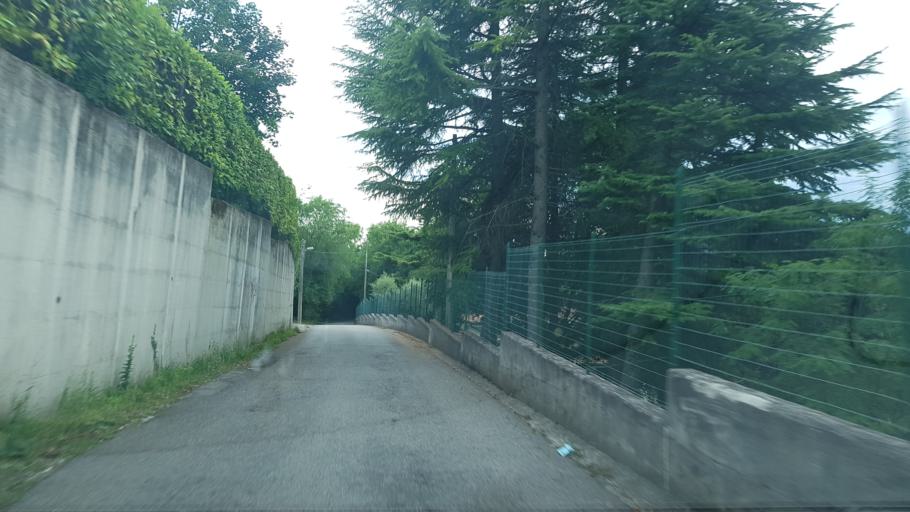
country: IT
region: Friuli Venezia Giulia
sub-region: Provincia di Gorizia
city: Gorizia
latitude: 45.9584
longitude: 13.6188
